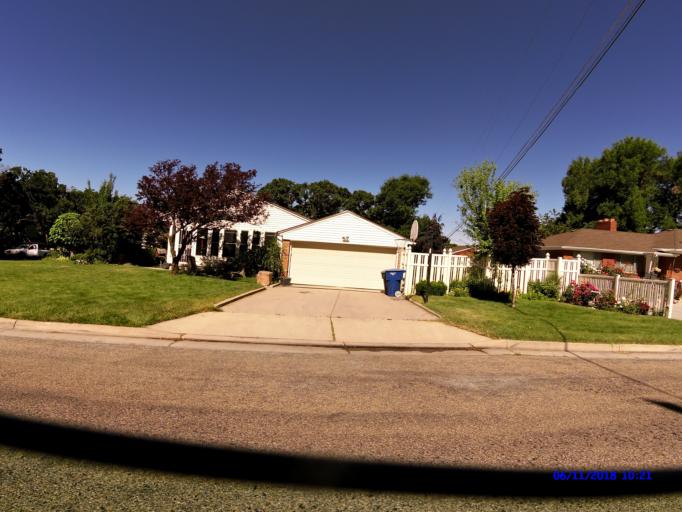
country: US
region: Utah
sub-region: Weber County
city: South Ogden
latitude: 41.2007
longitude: -111.9438
